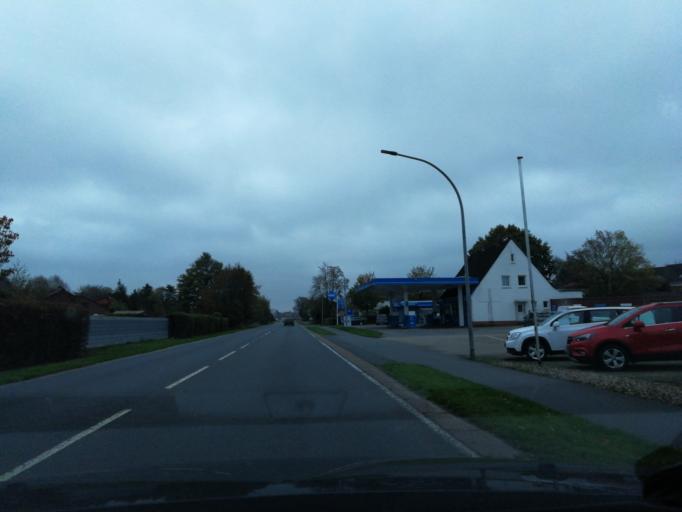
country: DE
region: Lower Saxony
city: Schortens
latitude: 53.5427
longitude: 7.9523
